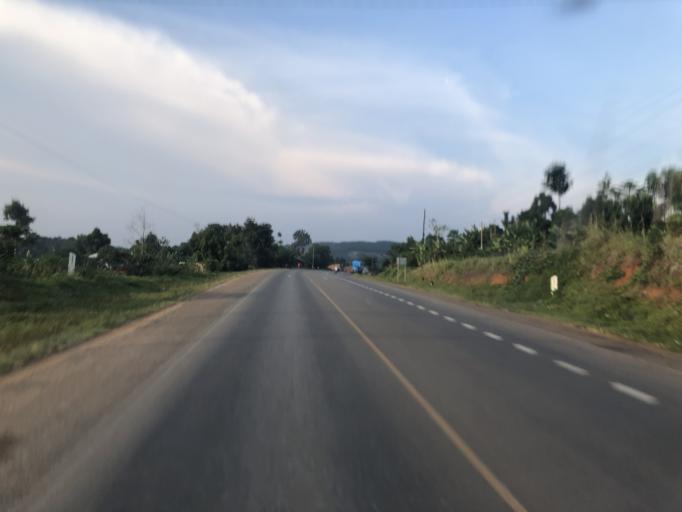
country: UG
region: Central Region
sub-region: Mpigi District
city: Mpigi
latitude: 0.2003
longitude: 32.3001
